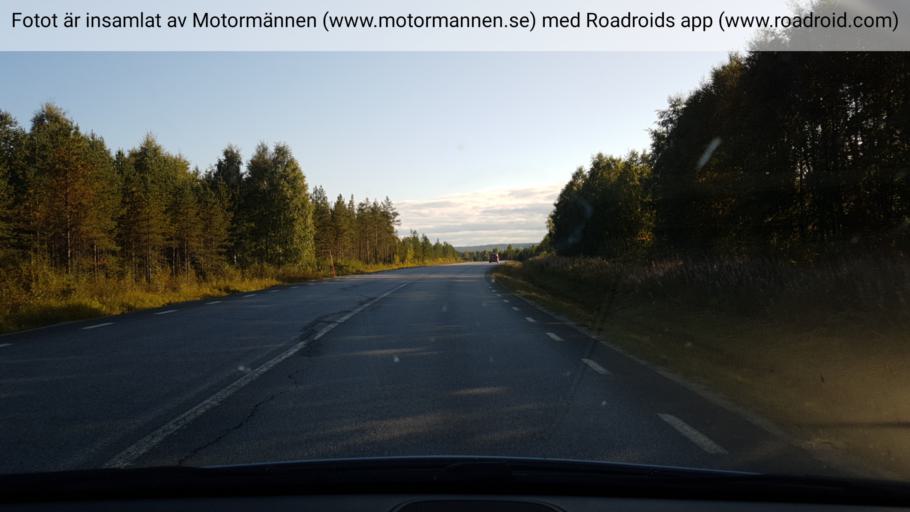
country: SE
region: Vaesterbotten
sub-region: Vannas Kommun
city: Vaennaes
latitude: 63.9888
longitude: 19.7320
